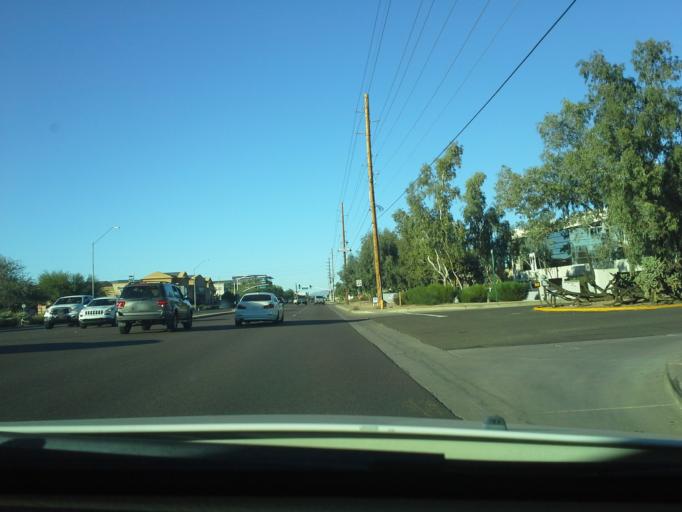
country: US
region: Arizona
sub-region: Maricopa County
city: Paradise Valley
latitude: 33.6158
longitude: -111.9257
